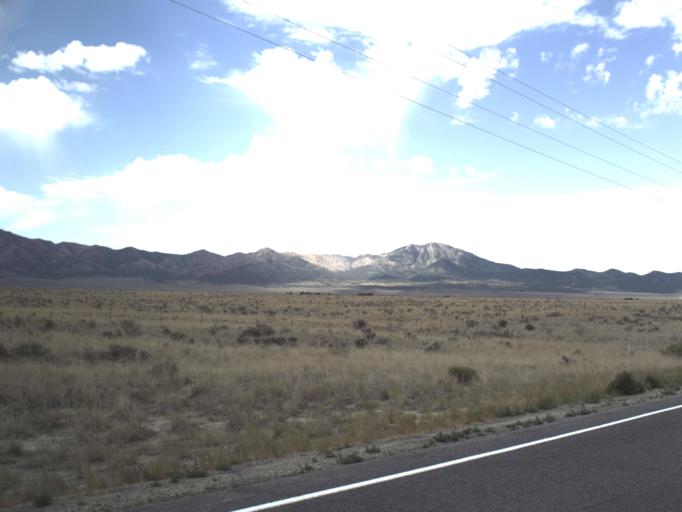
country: US
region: Utah
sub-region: Tooele County
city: Tooele
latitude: 40.0819
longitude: -112.4095
